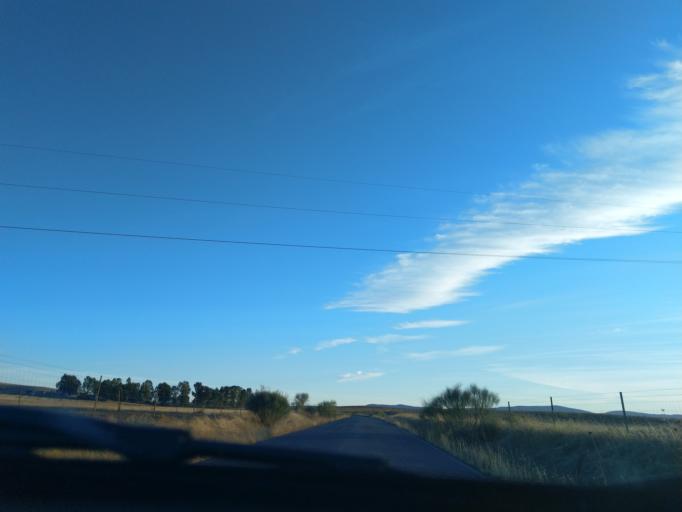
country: ES
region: Extremadura
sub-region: Provincia de Badajoz
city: Ahillones
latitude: 38.2594
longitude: -5.8263
